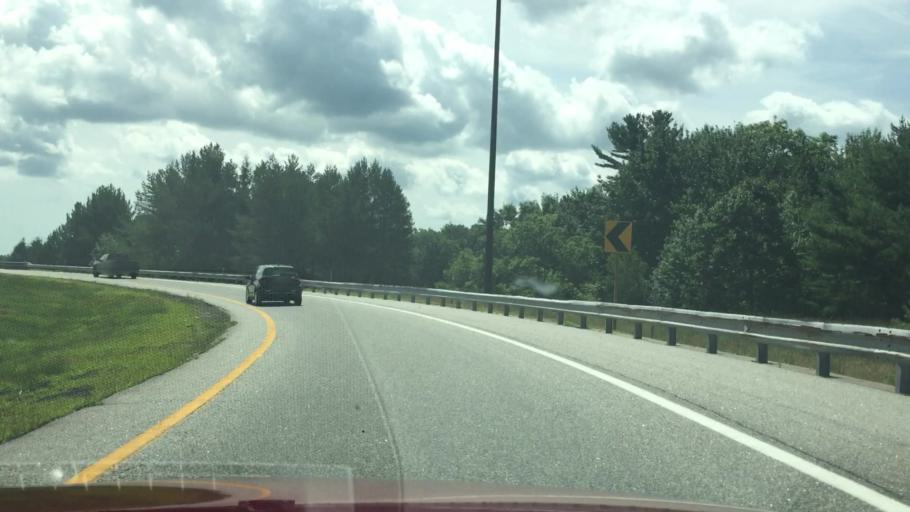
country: US
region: Maine
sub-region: York County
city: Saco
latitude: 43.5285
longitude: -70.4543
